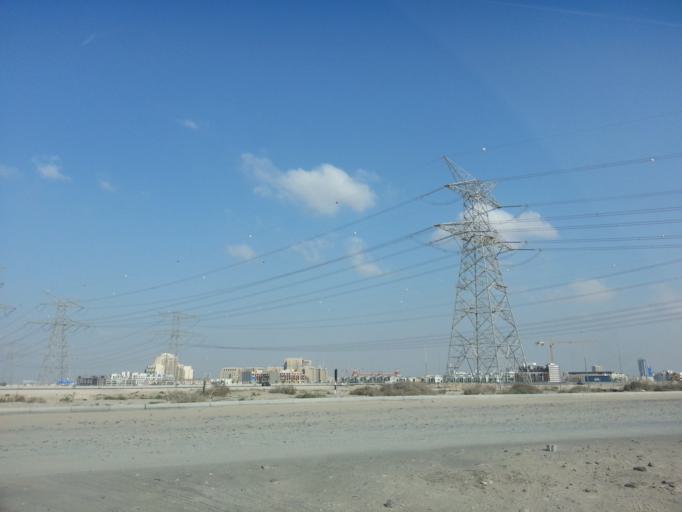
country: AE
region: Dubai
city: Dubai
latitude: 25.0641
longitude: 55.1949
